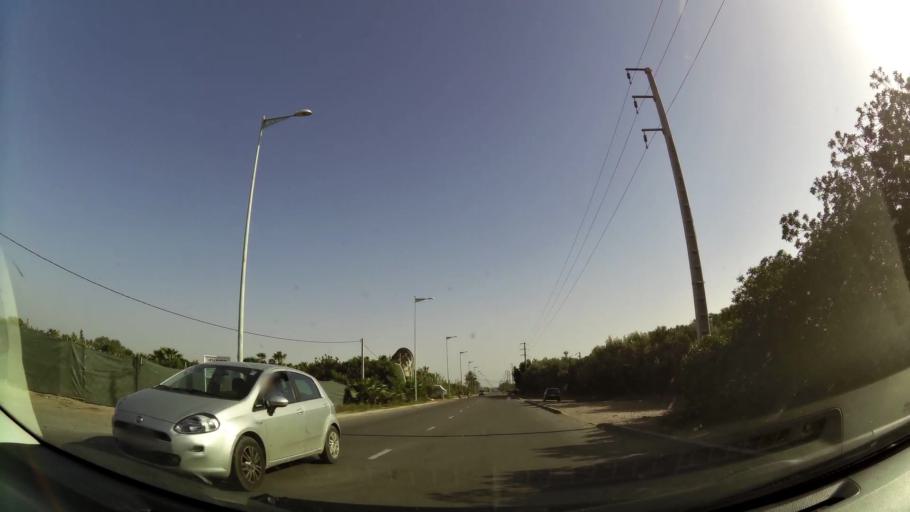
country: MA
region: Souss-Massa-Draa
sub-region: Inezgane-Ait Mellou
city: Inezgane
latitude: 30.3668
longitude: -9.5061
